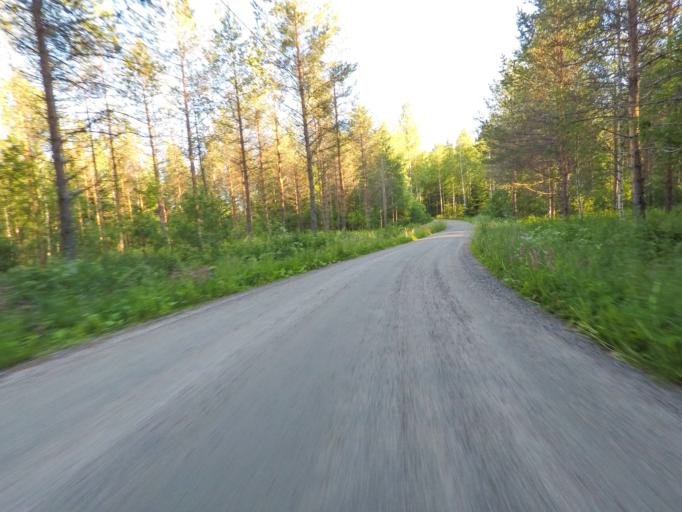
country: FI
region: Northern Savo
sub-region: Kuopio
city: Maaninka
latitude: 62.8817
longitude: 27.2940
